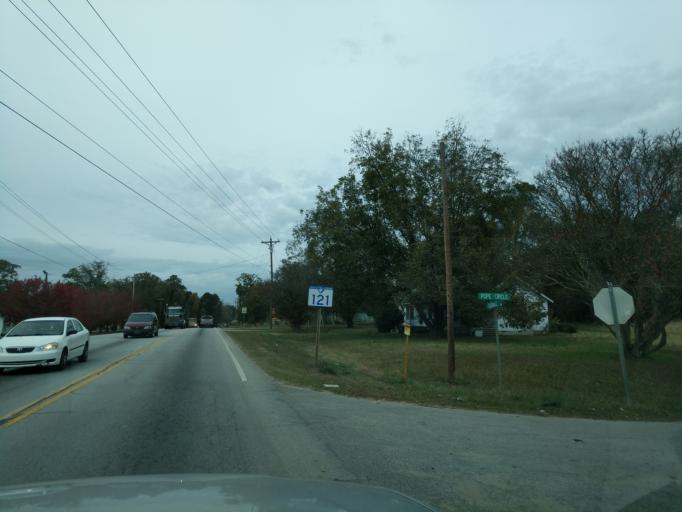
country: US
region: South Carolina
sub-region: Newberry County
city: Newberry
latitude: 34.2828
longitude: -81.6371
